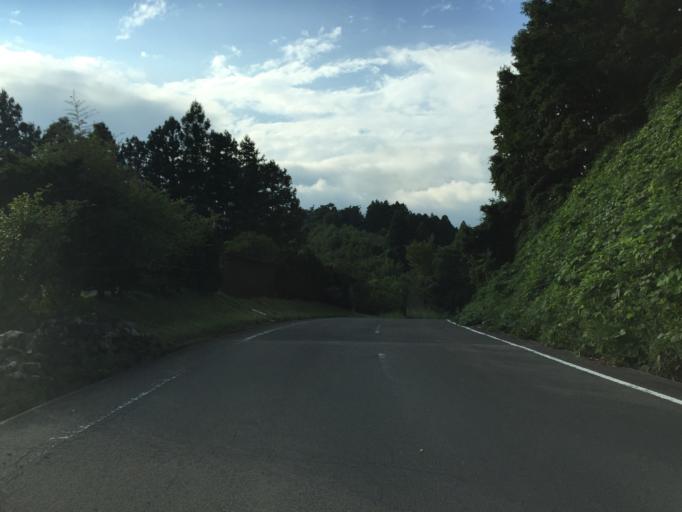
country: JP
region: Fukushima
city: Fukushima-shi
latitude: 37.6576
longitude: 140.5529
